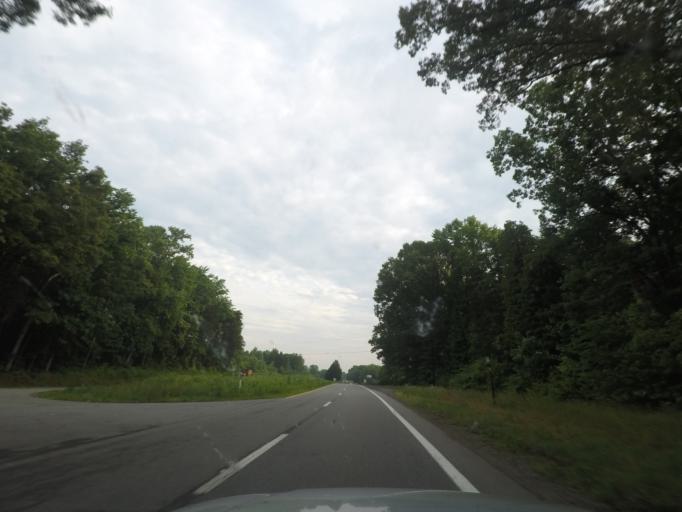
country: US
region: Virginia
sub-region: Halifax County
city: Halifax
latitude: 36.7730
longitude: -78.8152
